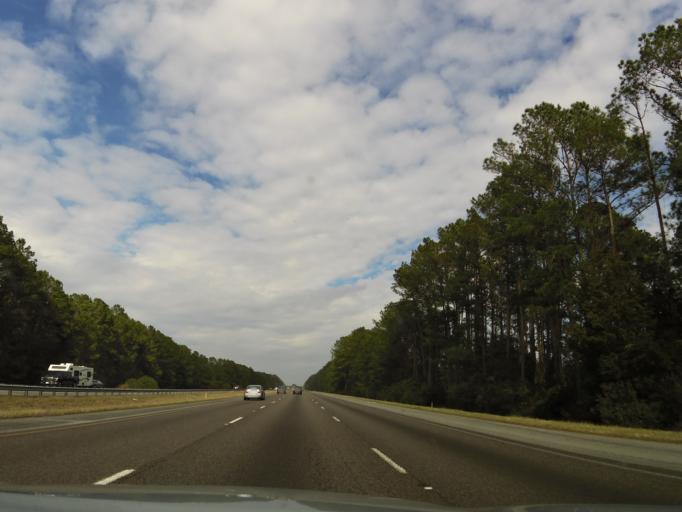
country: US
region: Georgia
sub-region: Liberty County
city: Midway
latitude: 31.8452
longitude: -81.3464
